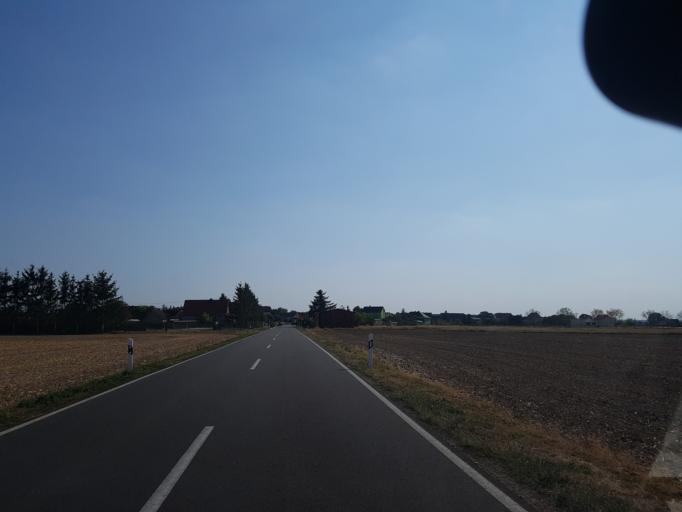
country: DE
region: Saxony-Anhalt
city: Prettin
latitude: 51.6512
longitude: 12.9850
